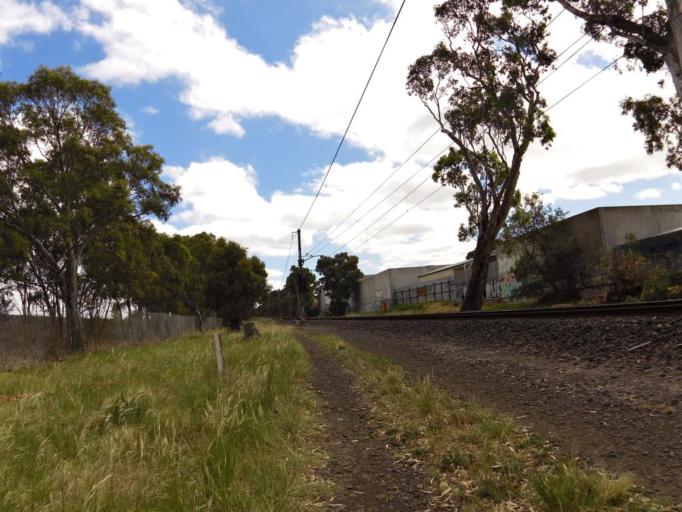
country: AU
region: Victoria
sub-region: Hume
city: Campbellfield
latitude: -37.6977
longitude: 144.9584
